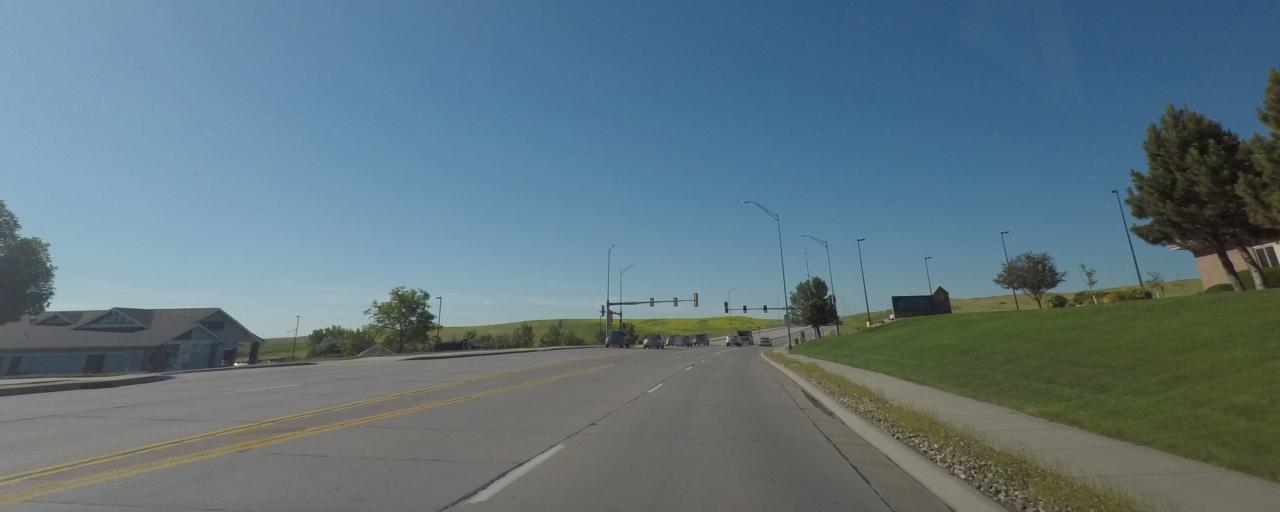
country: US
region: South Dakota
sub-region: Pennington County
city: Rapid City
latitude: 44.0439
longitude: -103.2194
